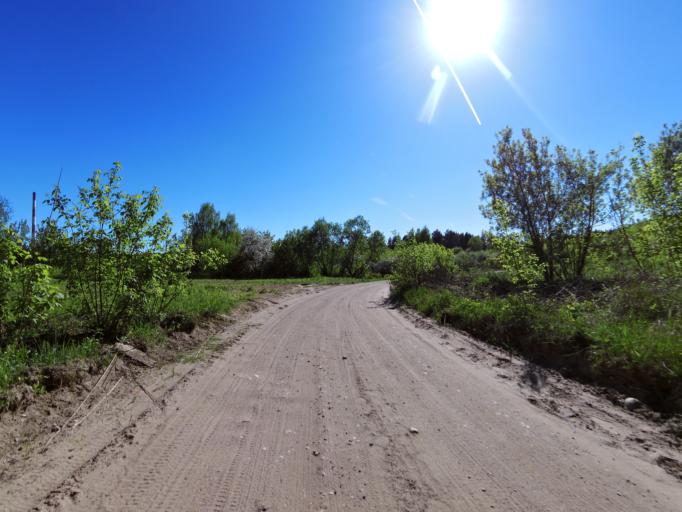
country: LT
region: Vilnius County
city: Pilaite
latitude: 54.6823
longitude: 25.1562
